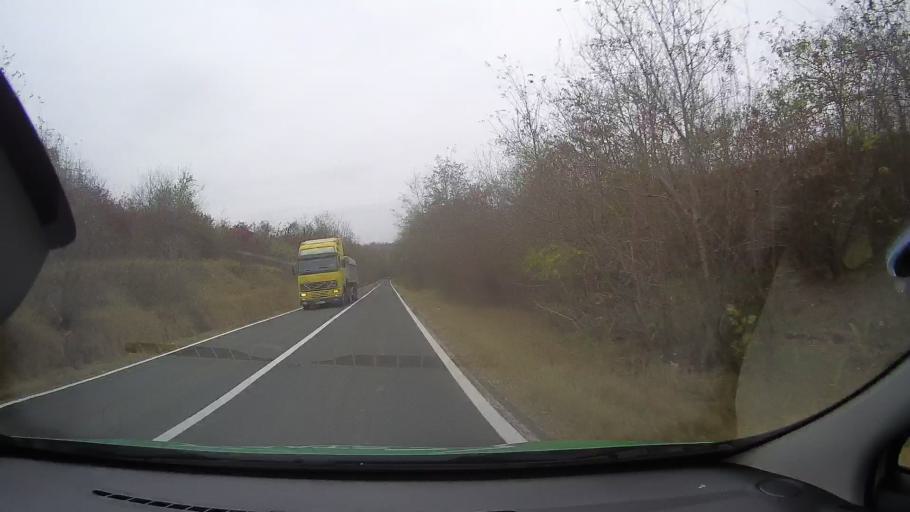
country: RO
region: Constanta
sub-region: Comuna Garliciu
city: Garliciu
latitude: 44.7099
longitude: 28.0764
